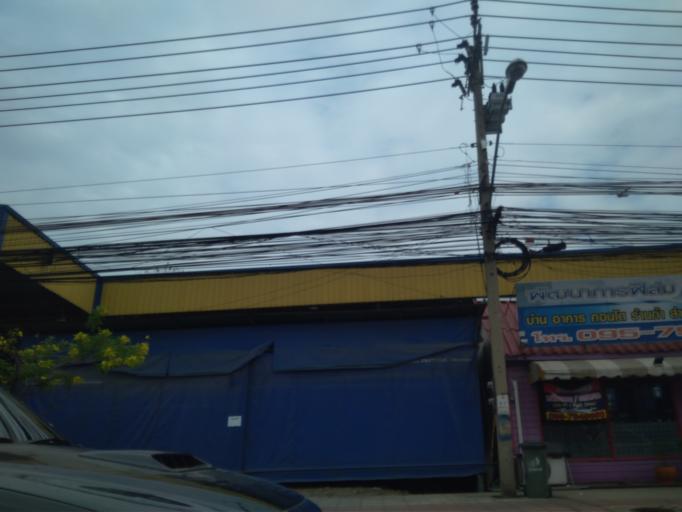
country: TH
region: Bangkok
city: Suan Luang
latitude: 13.7012
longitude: 100.6465
